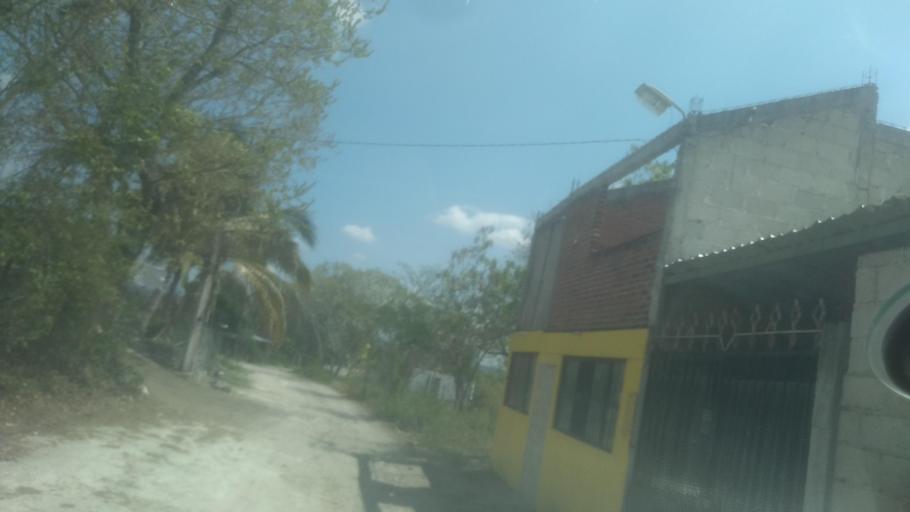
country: MX
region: Veracruz
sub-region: Emiliano Zapata
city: Plan del Rio
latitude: 19.3961
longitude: -96.6350
